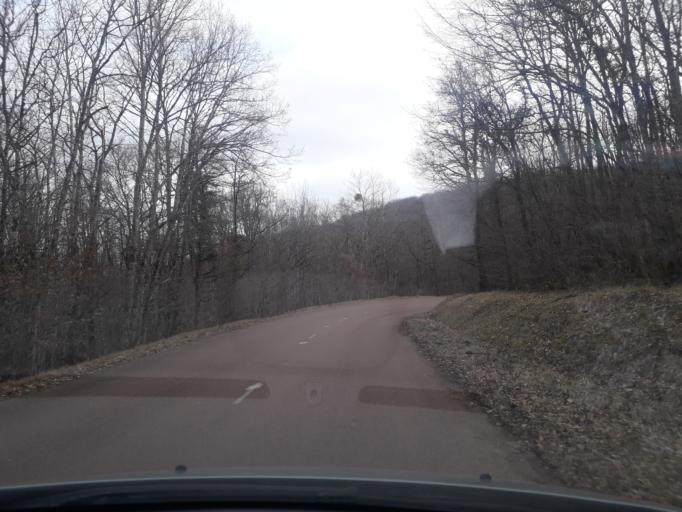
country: FR
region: Bourgogne
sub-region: Departement de la Cote-d'Or
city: Messigny-et-Vantoux
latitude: 47.4665
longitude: 4.9411
